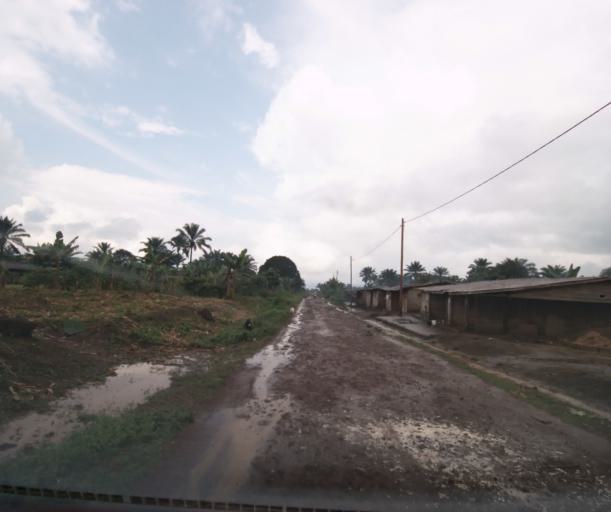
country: CM
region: Littoral
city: Melong
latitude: 5.0580
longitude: 9.9611
